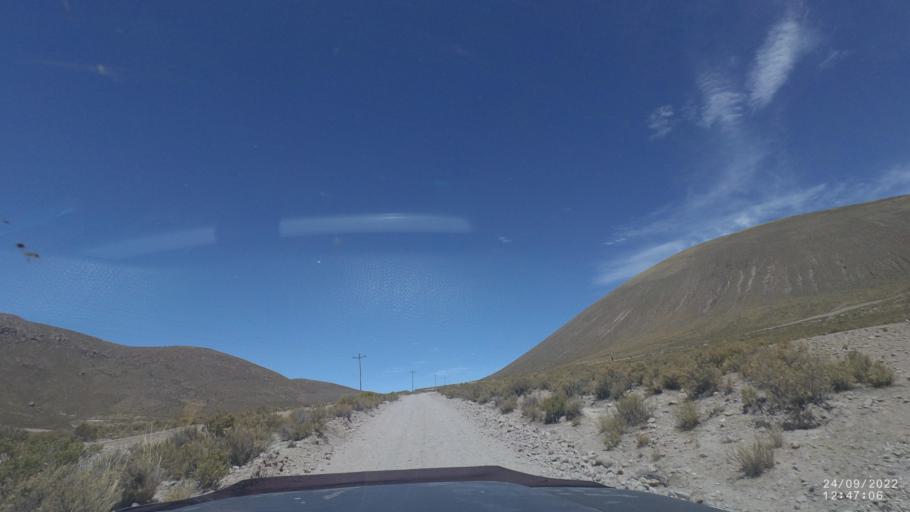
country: BO
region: Potosi
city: Colchani
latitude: -19.8073
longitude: -67.5690
